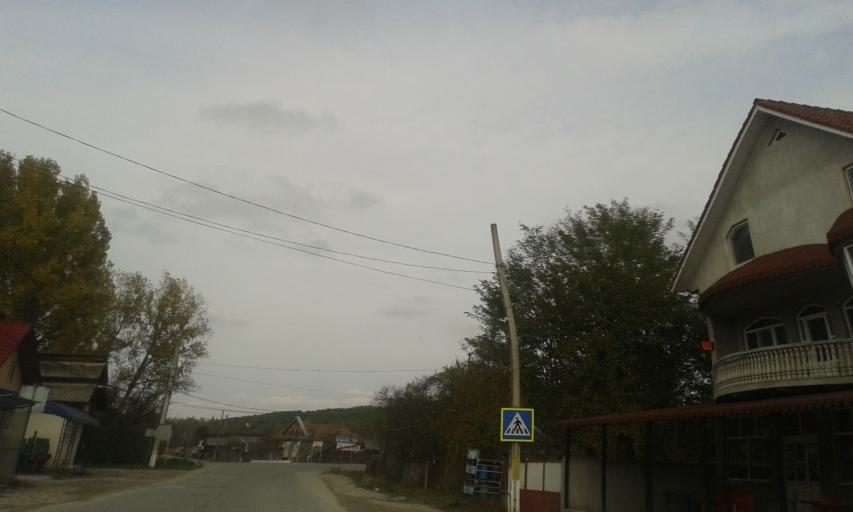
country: RO
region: Gorj
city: Logresti
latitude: 44.8867
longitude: 23.7135
